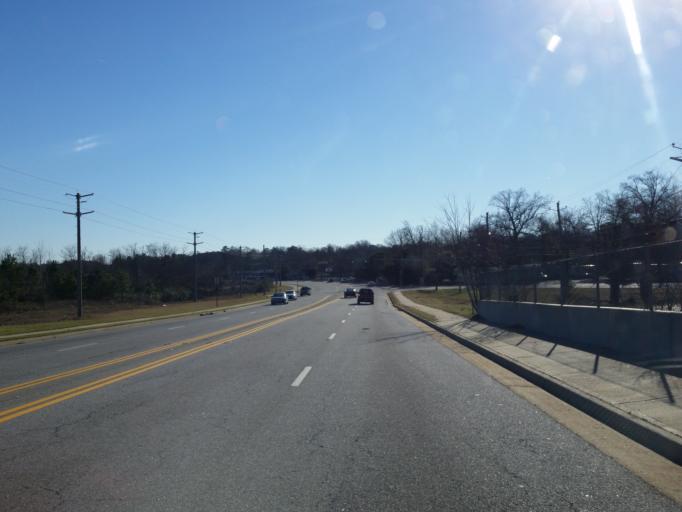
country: US
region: Georgia
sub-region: Cobb County
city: Fair Oaks
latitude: 33.9260
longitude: -84.5418
